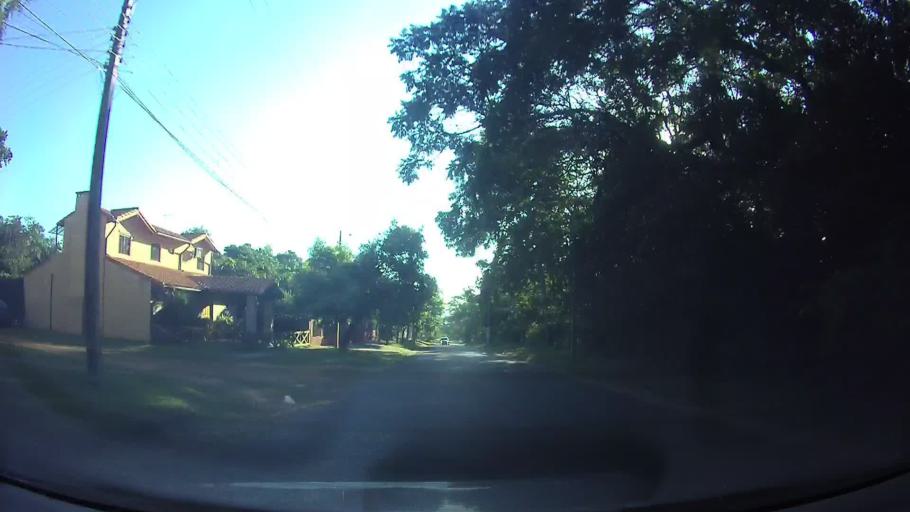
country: PY
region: Cordillera
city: San Bernardino
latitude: -25.3204
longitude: -57.2729
